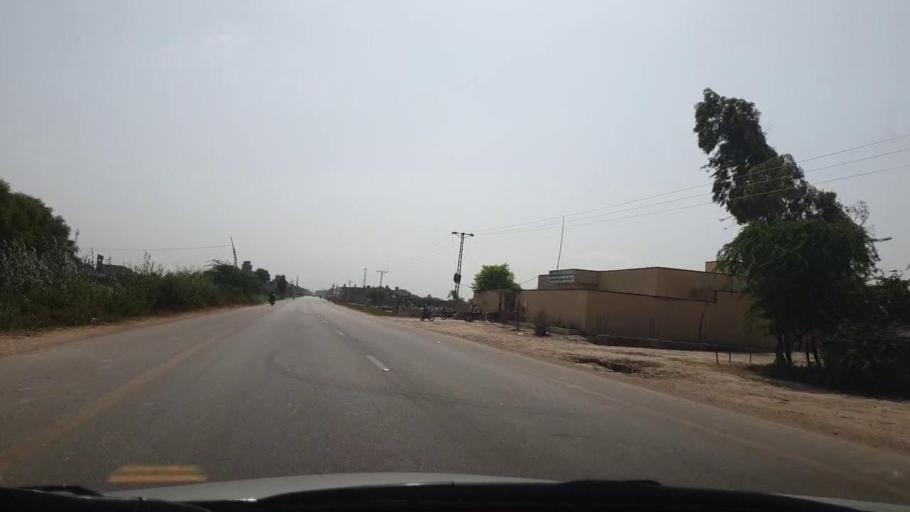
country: PK
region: Sindh
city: Matli
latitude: 25.0398
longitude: 68.6452
